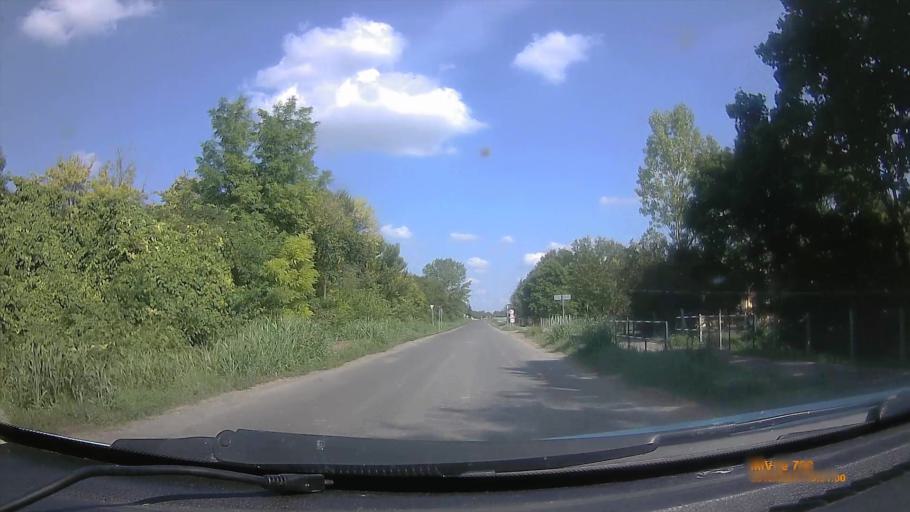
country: HU
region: Baranya
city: Szentlorinc
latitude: 46.0356
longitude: 18.0060
